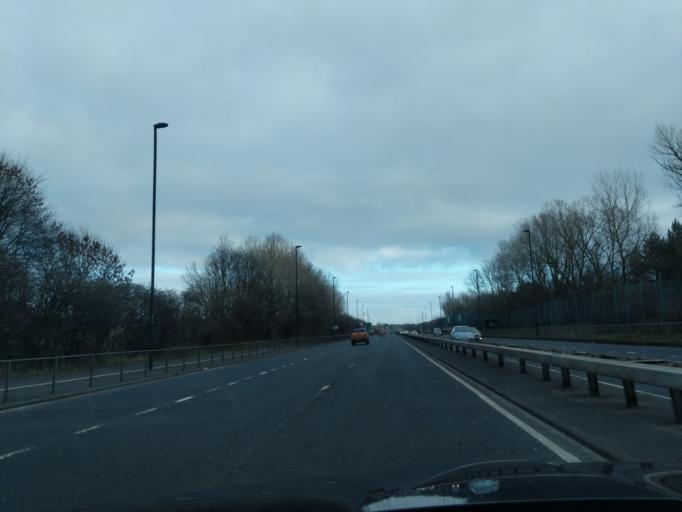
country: GB
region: England
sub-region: Borough of North Tyneside
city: Wallsend
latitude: 54.9976
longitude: -1.5540
